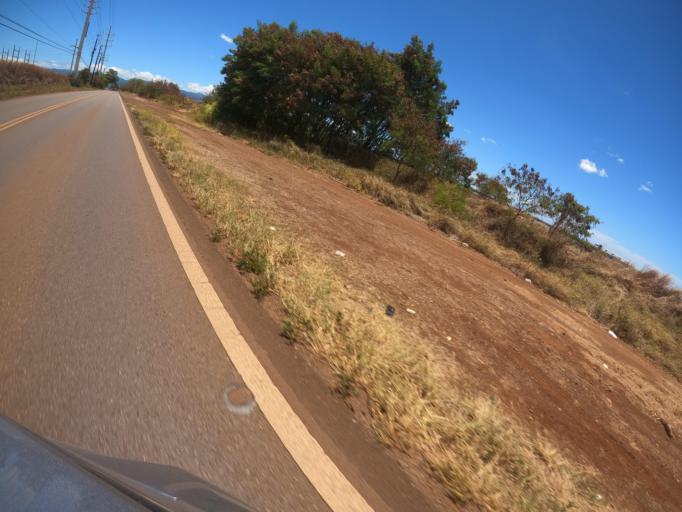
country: US
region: Hawaii
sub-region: Honolulu County
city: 'Ewa Villages
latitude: 21.3703
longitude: -158.0471
